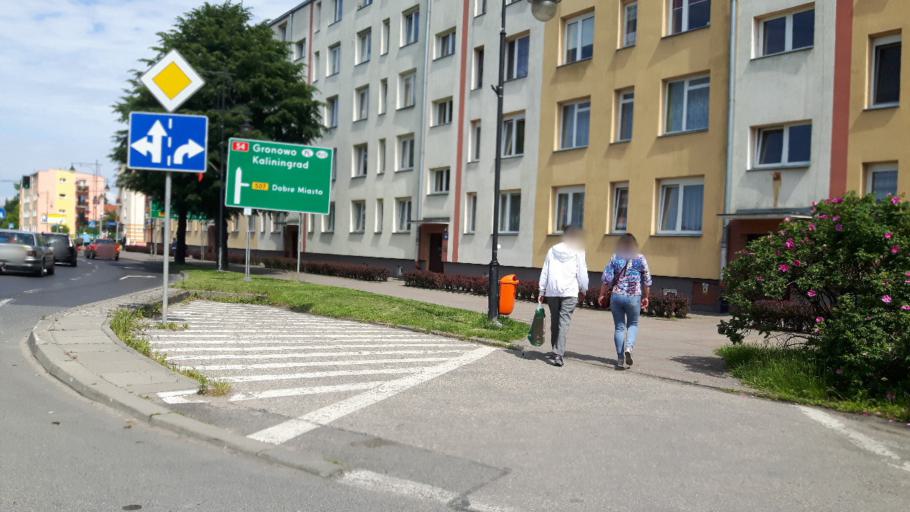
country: PL
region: Warmian-Masurian Voivodeship
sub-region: Powiat braniewski
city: Braniewo
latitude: 54.3835
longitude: 19.8272
